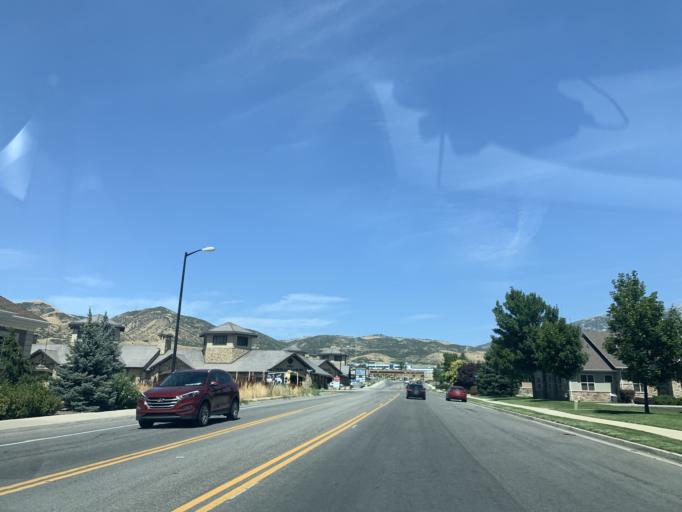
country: US
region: Utah
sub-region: Utah County
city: Lehi
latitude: 40.4284
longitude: -111.8305
